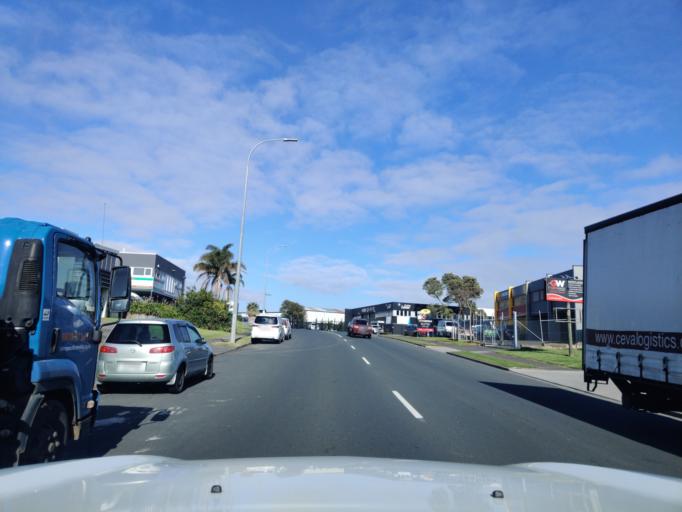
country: NZ
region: Auckland
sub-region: Auckland
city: Manukau City
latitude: -36.9444
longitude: 174.8816
